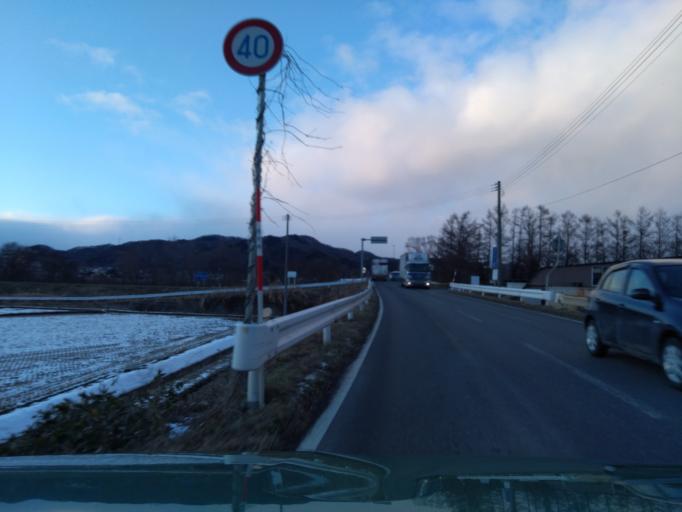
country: JP
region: Iwate
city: Shizukuishi
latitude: 39.6949
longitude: 141.0648
